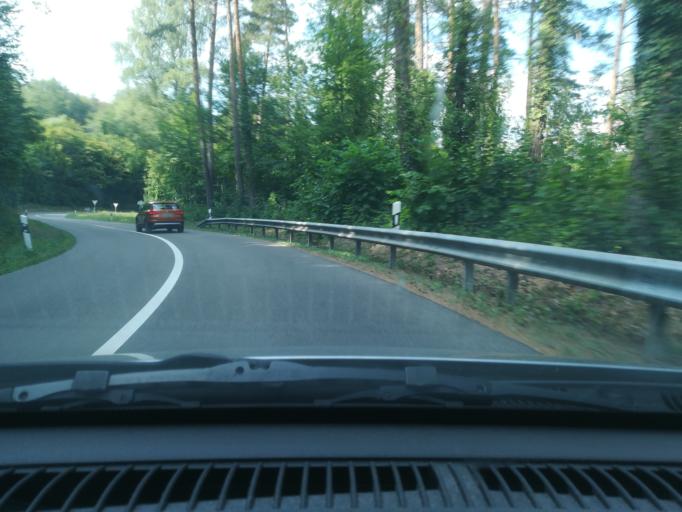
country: CH
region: Schaffhausen
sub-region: Bezirk Reiat
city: Thayngen
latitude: 47.7454
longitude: 8.6926
